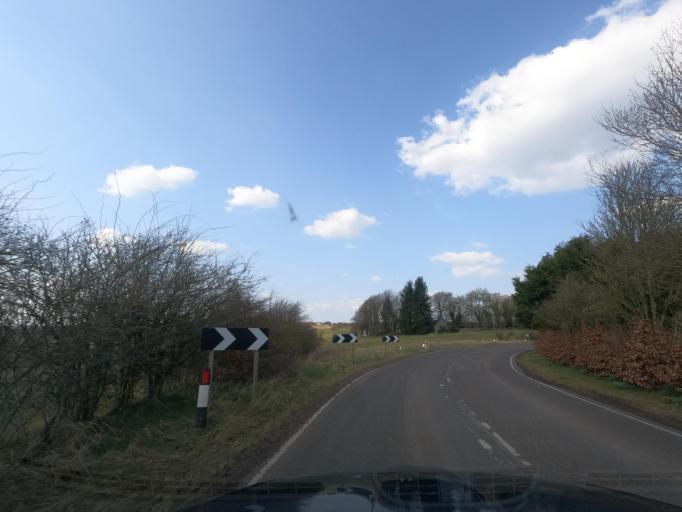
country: GB
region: Scotland
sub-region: South Lanarkshire
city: Forth
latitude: 55.7601
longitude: -3.6682
